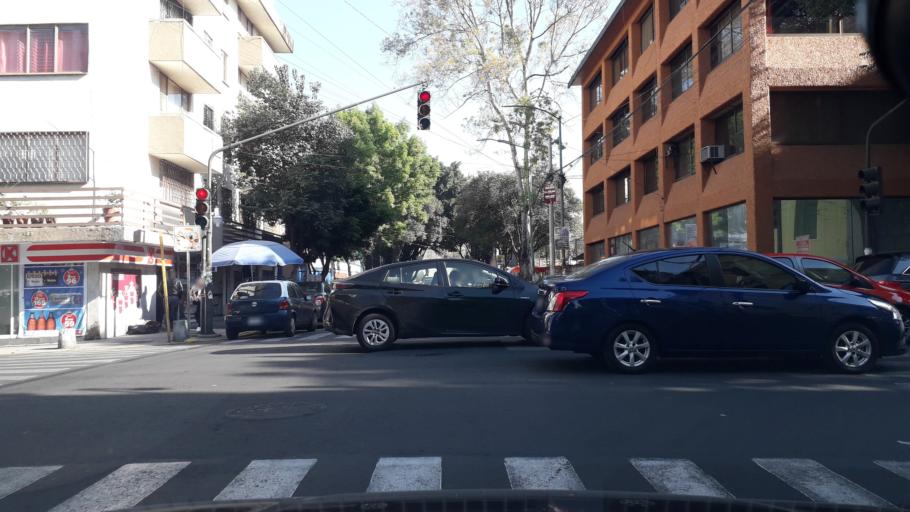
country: MX
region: Mexico City
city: Cuauhtemoc
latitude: 19.4384
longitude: -99.1575
